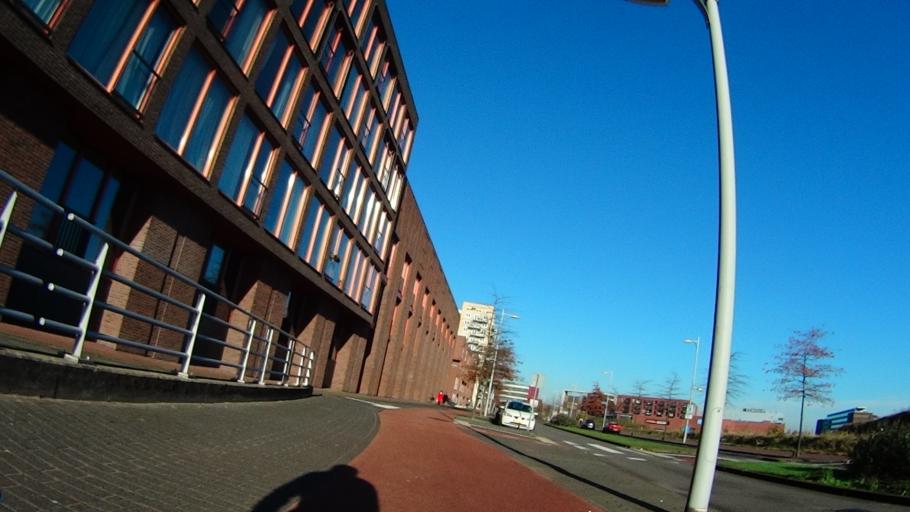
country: NL
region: Utrecht
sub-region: Gemeente Amersfoort
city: Amersfoort
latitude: 52.1559
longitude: 5.3788
